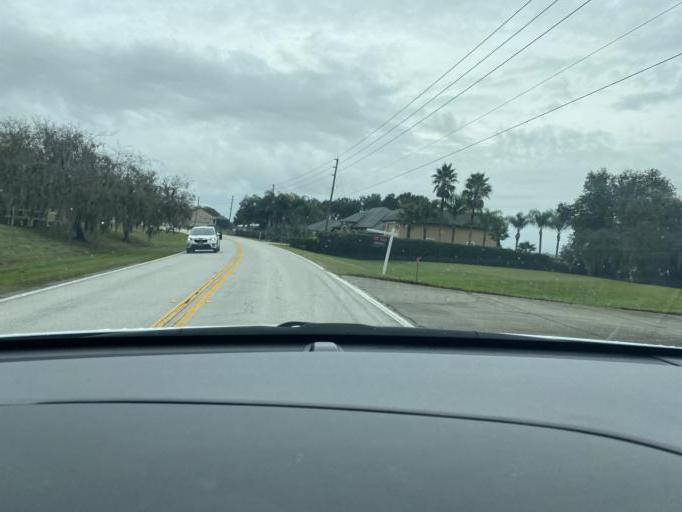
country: US
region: Florida
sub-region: Lake County
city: Clermont
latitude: 28.5835
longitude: -81.7811
